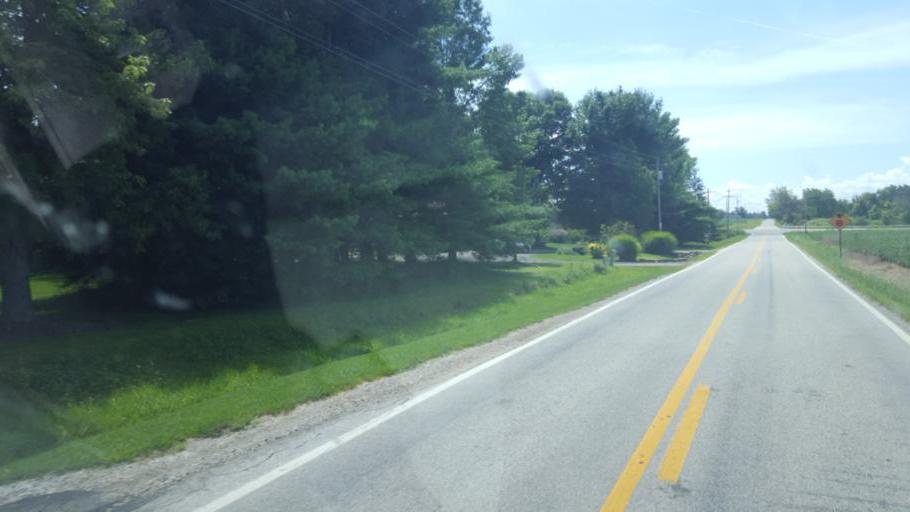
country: US
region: Ohio
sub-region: Knox County
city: Centerburg
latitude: 40.3199
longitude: -82.7953
